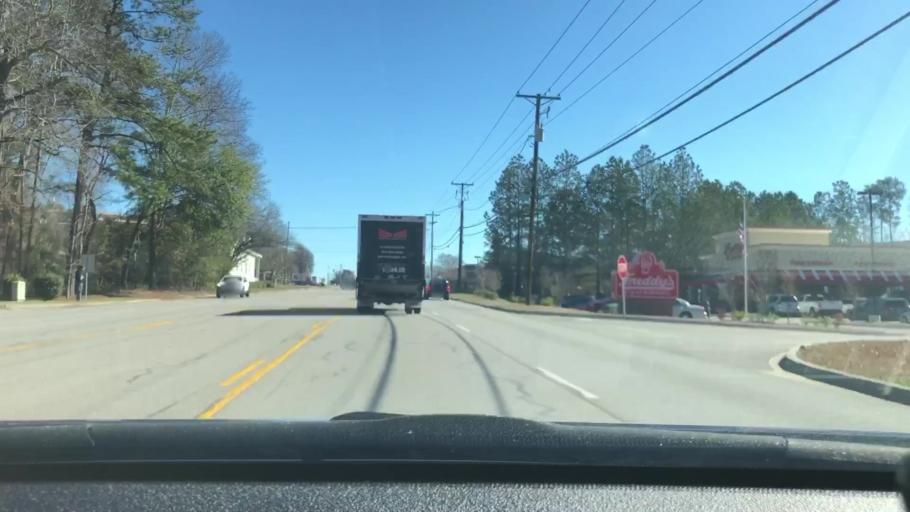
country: US
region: South Carolina
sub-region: Lexington County
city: Oak Grove
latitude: 34.0056
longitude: -81.1194
